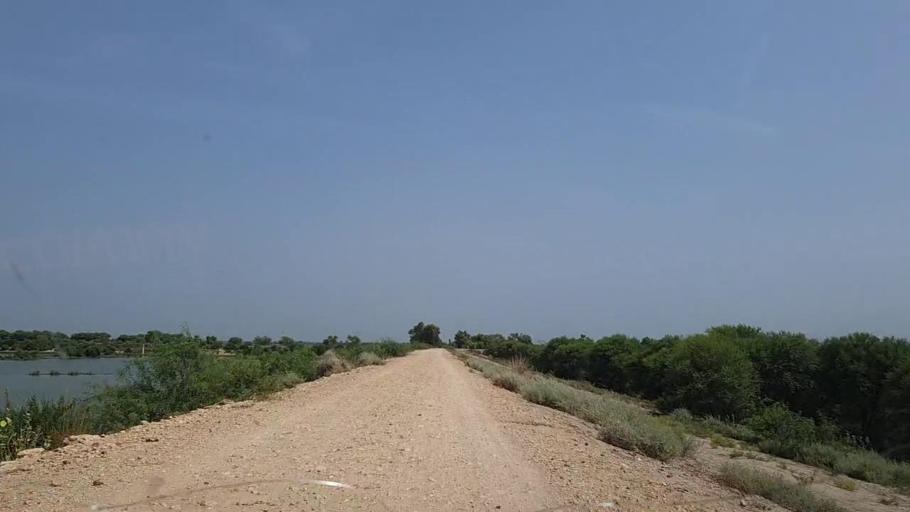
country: PK
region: Sindh
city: Ghotki
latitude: 28.0904
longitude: 69.4094
